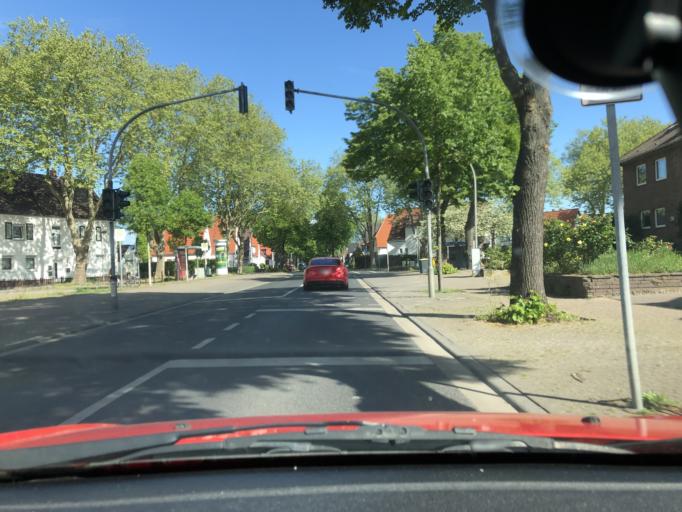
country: DE
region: North Rhine-Westphalia
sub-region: Regierungsbezirk Dusseldorf
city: Kamp-Lintfort
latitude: 51.4942
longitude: 6.5566
